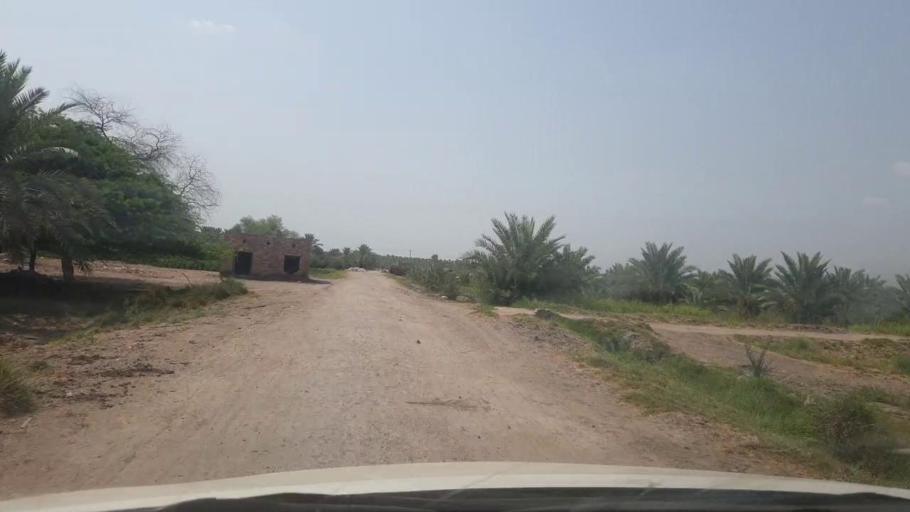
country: PK
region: Sindh
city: Khairpur
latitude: 27.5625
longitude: 68.8464
